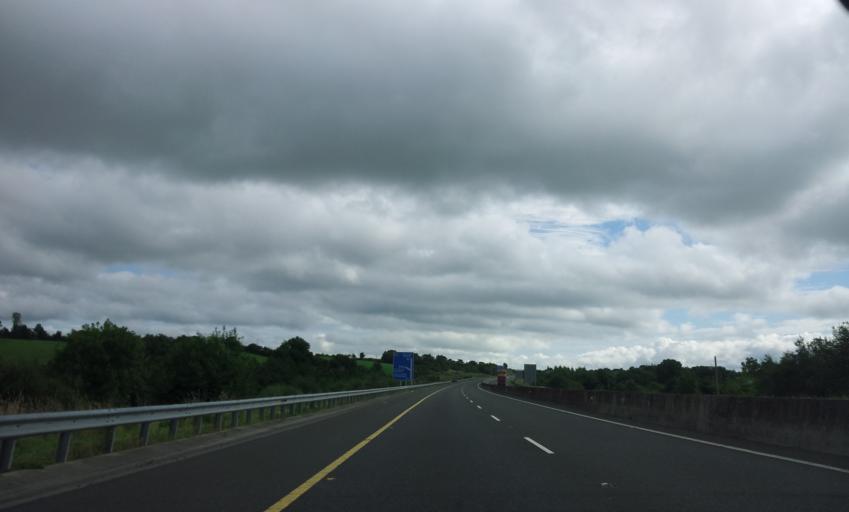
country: IE
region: Munster
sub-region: North Tipperary
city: Nenagh
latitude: 52.8559
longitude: -8.1367
